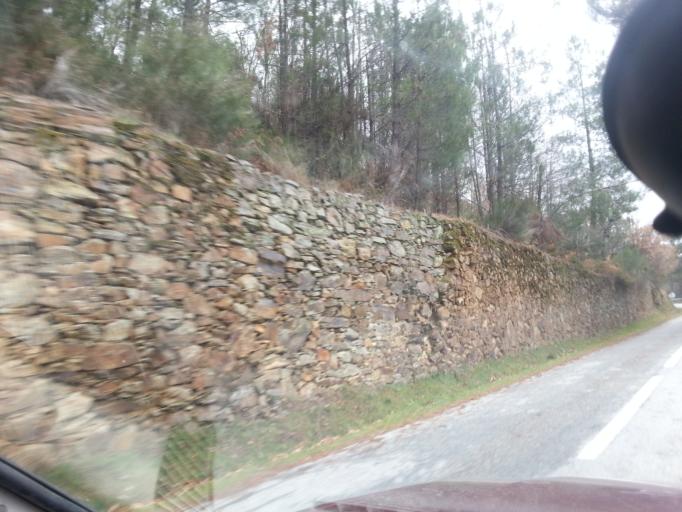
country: PT
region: Guarda
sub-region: Manteigas
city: Manteigas
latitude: 40.4120
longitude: -7.5260
